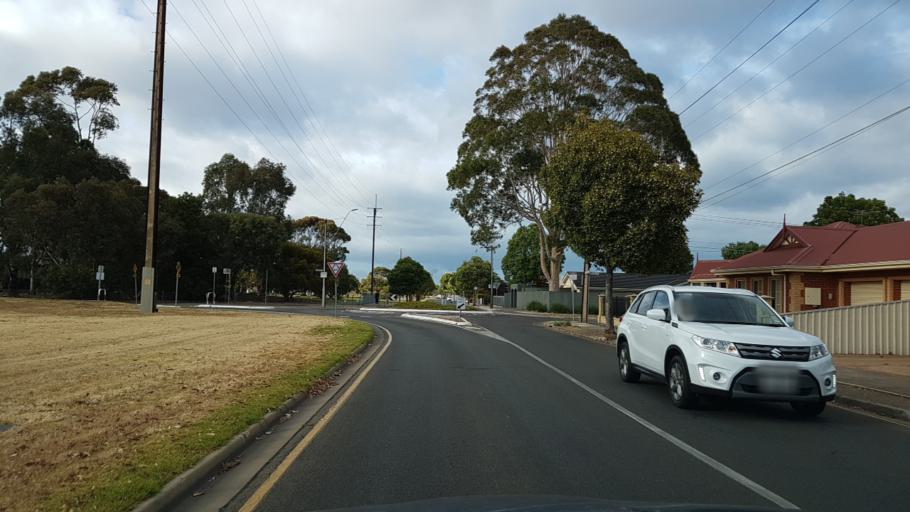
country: AU
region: South Australia
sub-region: City of West Torrens
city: Plympton
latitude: -34.9518
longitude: 138.5607
